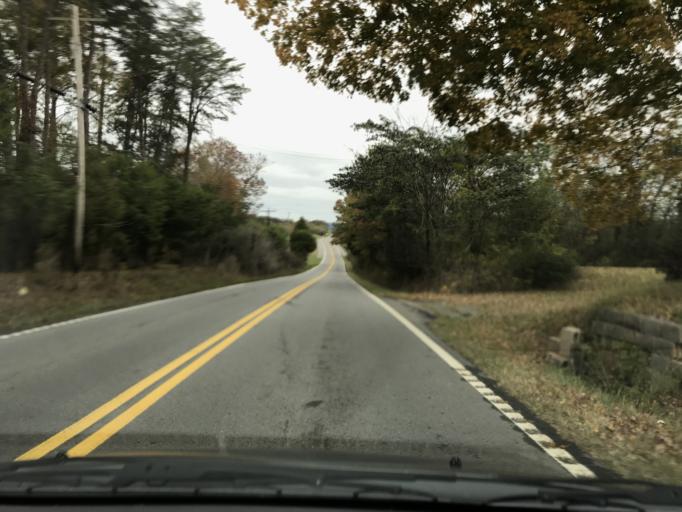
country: US
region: Tennessee
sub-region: Hamilton County
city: Sale Creek
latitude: 35.3767
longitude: -84.9982
